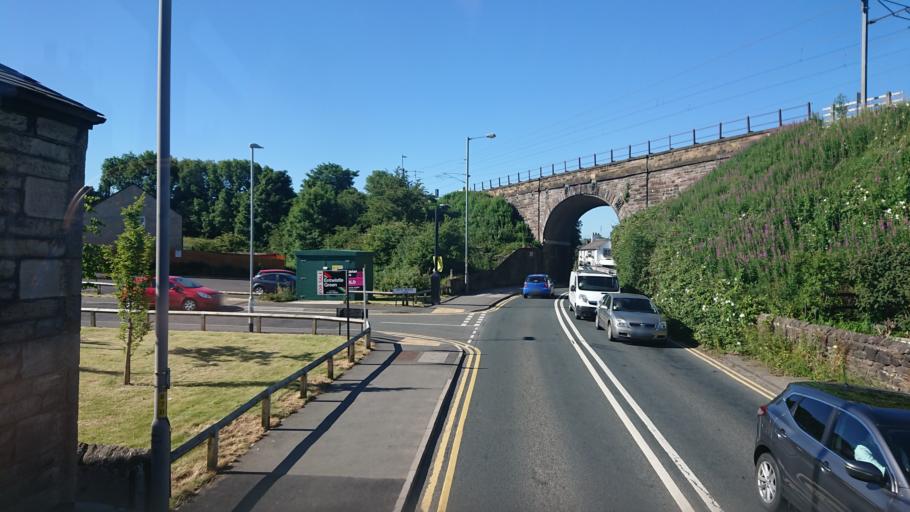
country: GB
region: England
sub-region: Lancashire
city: Galgate
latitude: 53.9908
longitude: -2.7893
